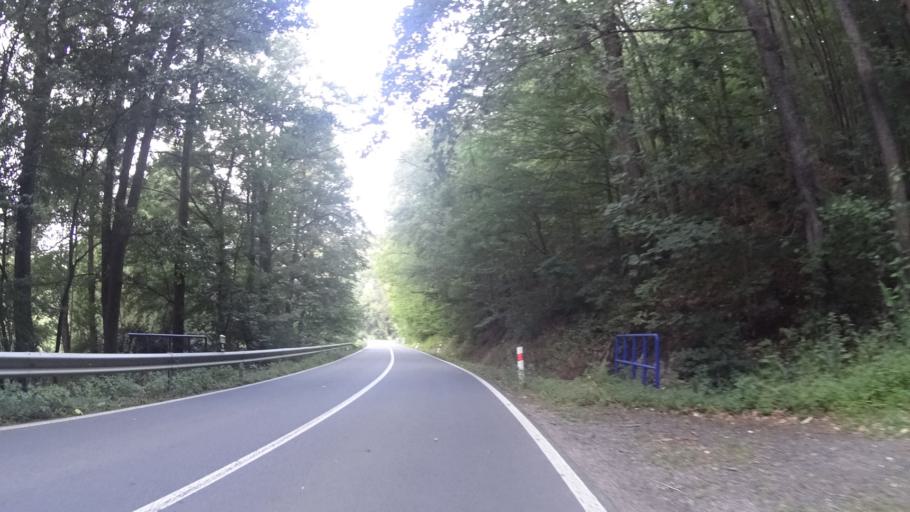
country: CZ
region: Olomoucky
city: Stity
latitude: 49.8659
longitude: 16.7368
